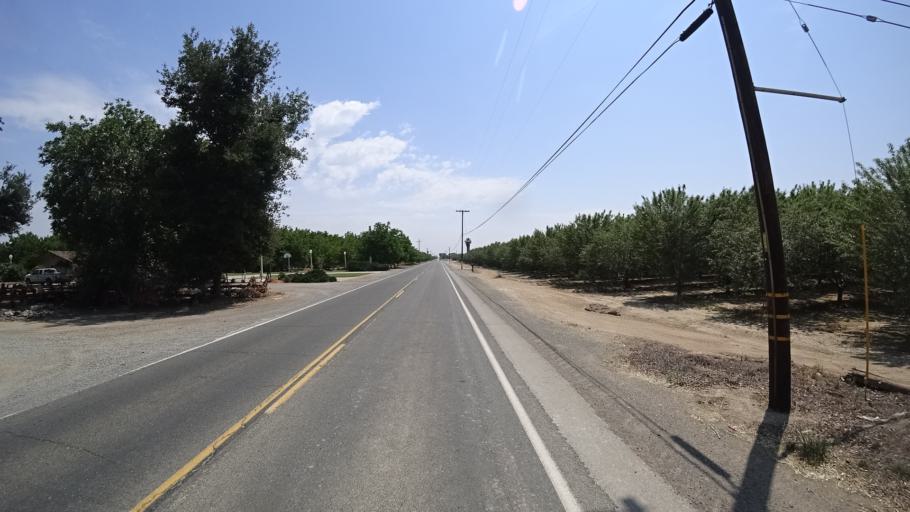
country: US
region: California
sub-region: Kings County
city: Armona
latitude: 36.3281
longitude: -119.7360
